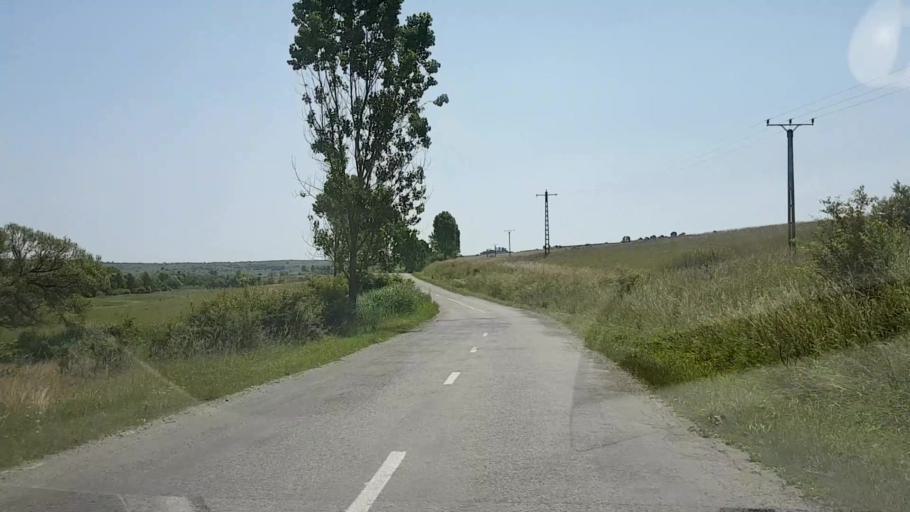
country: RO
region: Sibiu
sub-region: Comuna Merghindeal
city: Merghindeal
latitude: 45.9614
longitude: 24.7524
